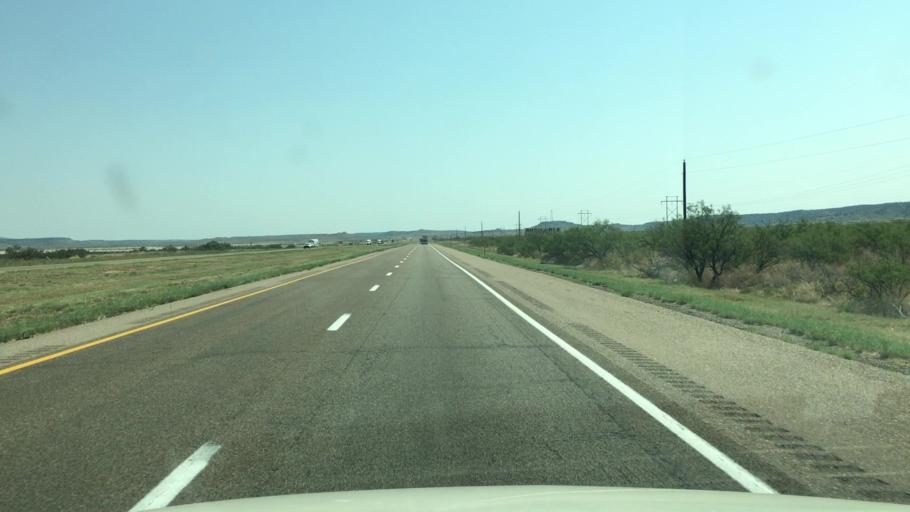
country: US
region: New Mexico
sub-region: Quay County
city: Tucumcari
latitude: 35.1134
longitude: -103.9981
